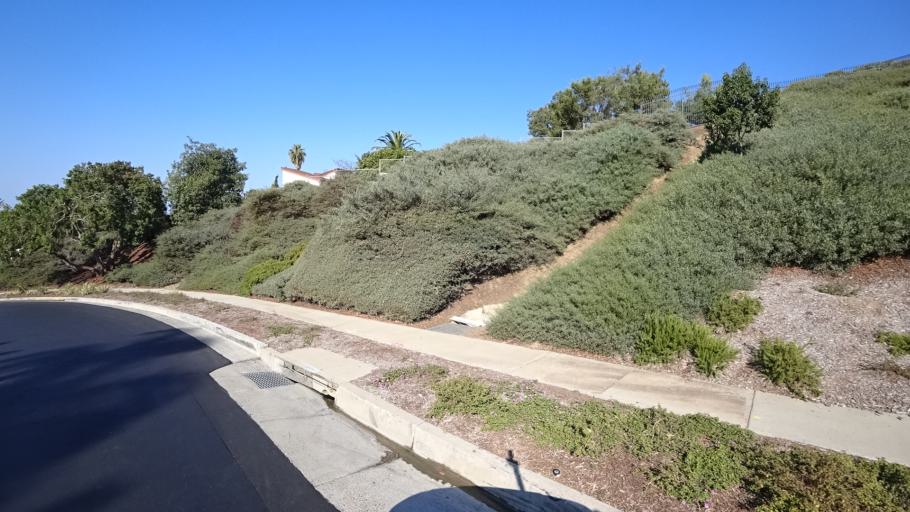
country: US
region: California
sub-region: Orange County
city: San Juan Capistrano
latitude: 33.4632
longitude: -117.6500
